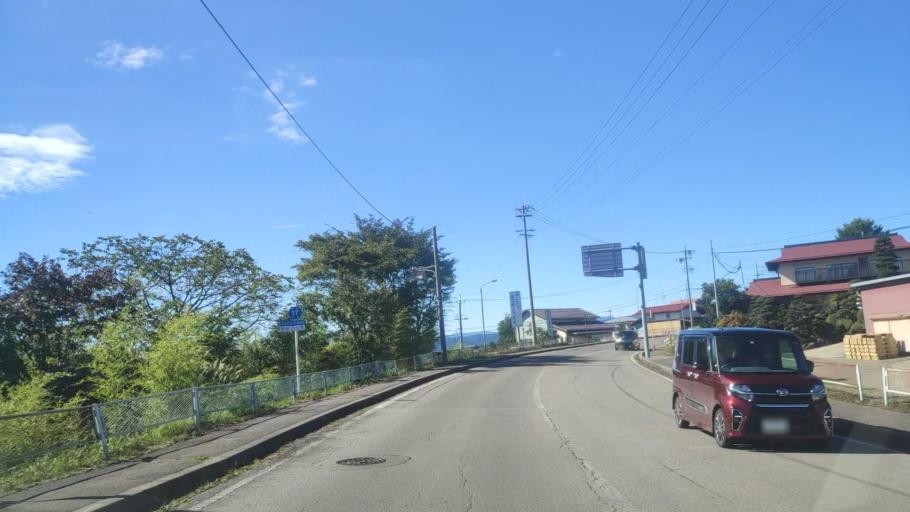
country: JP
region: Nagano
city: Chino
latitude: 35.9729
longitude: 138.2205
